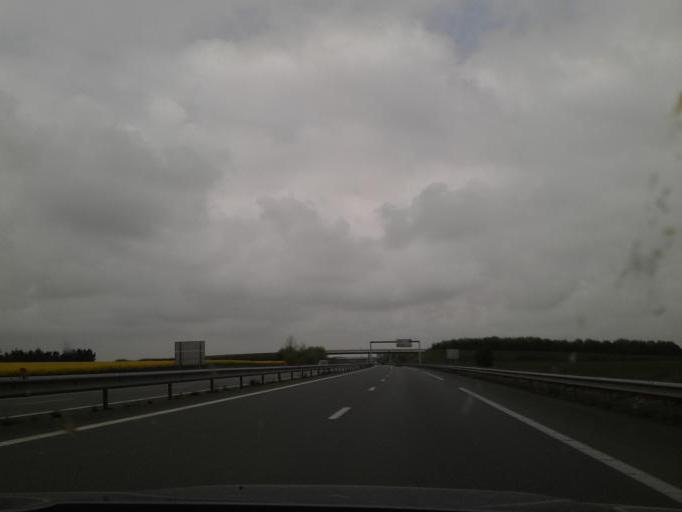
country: FR
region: Pays de la Loire
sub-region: Departement de la Vendee
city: Fontenay-le-Comte
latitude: 46.4322
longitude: -0.8092
